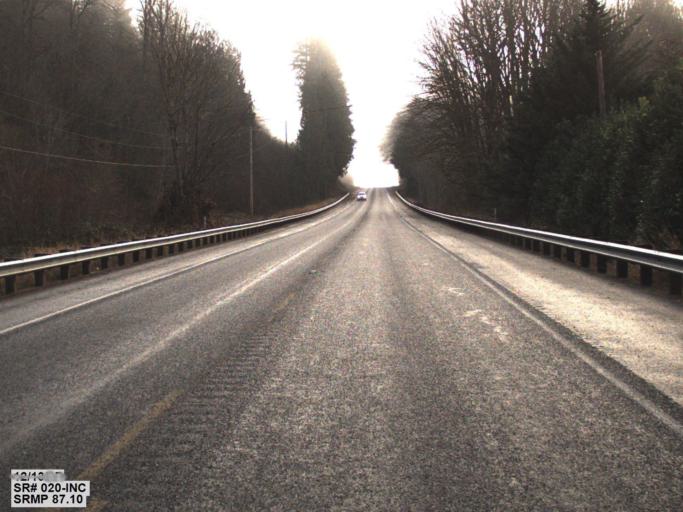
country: US
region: Washington
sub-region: Snohomish County
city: Darrington
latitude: 48.5424
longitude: -121.7886
